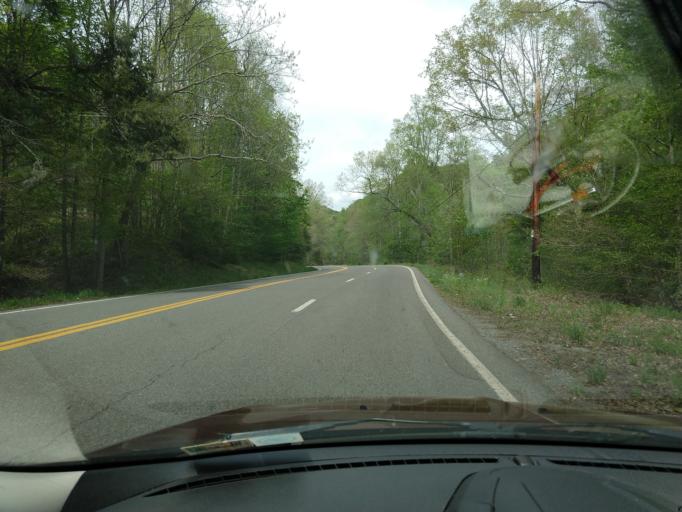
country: US
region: West Virginia
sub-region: McDowell County
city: Welch
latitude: 37.3543
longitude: -81.6627
